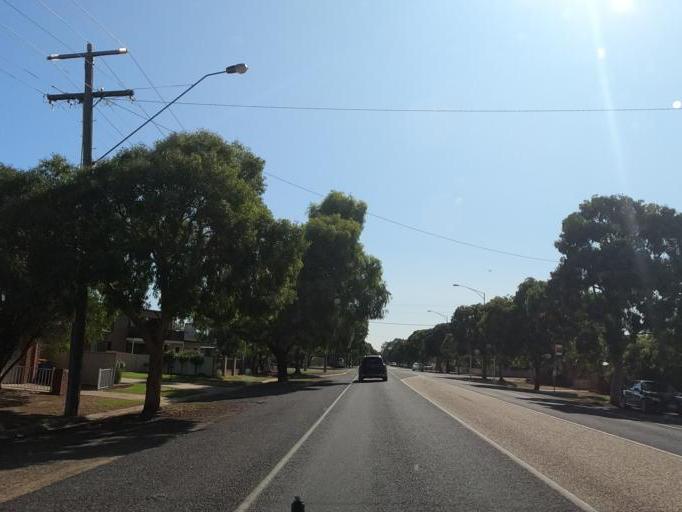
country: AU
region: Victoria
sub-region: Moira
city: Yarrawonga
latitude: -36.0171
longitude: 146.0064
